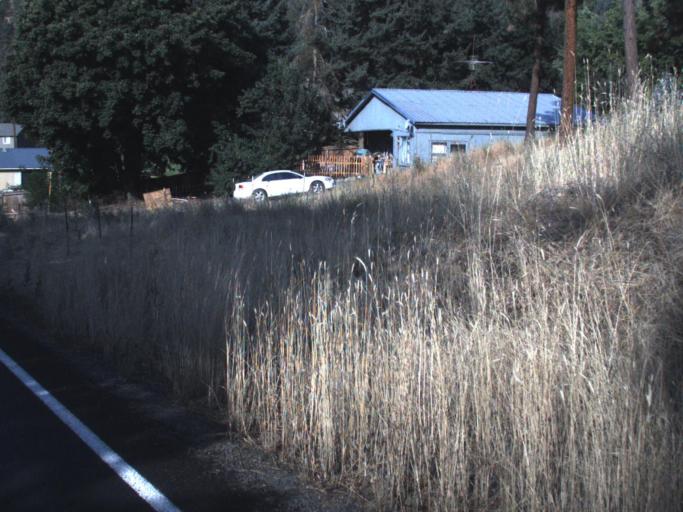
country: US
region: Washington
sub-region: Spokane County
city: Deer Park
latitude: 47.8919
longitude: -117.6809
